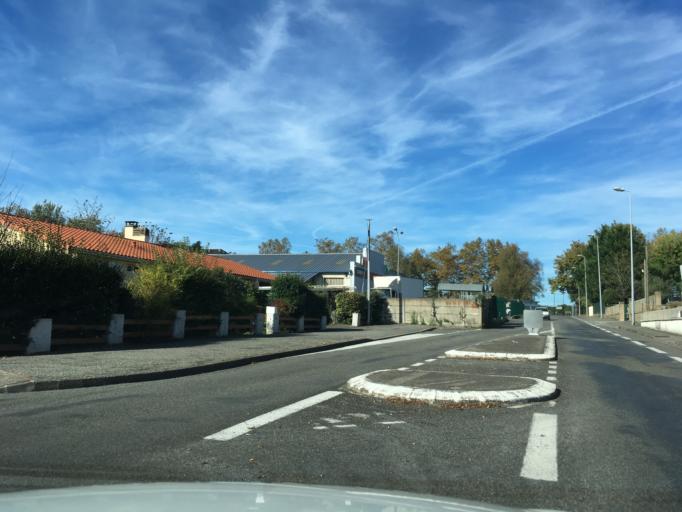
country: FR
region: Aquitaine
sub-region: Departement des Pyrenees-Atlantiques
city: Pau
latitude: 43.3299
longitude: -0.3613
